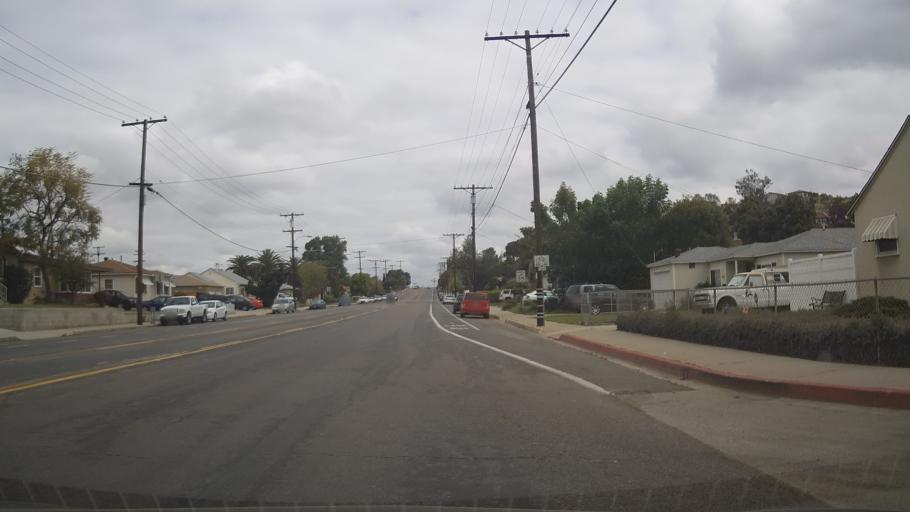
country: US
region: California
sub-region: San Diego County
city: Lemon Grove
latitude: 32.7470
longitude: -117.0428
